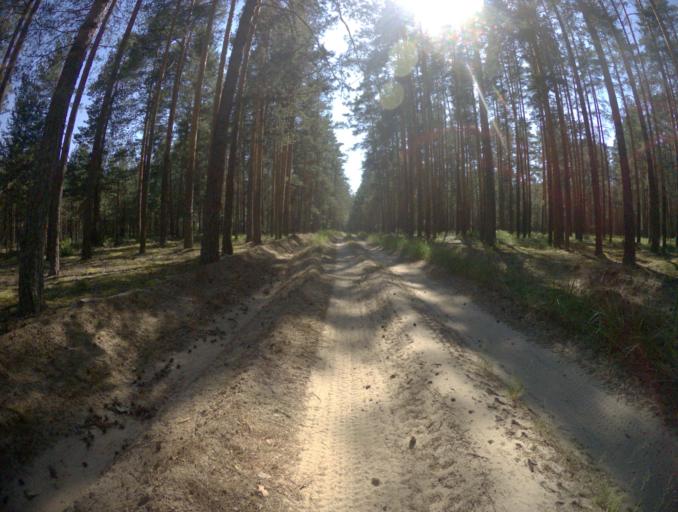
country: RU
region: Vladimir
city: Vyazniki
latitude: 56.3763
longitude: 42.1987
